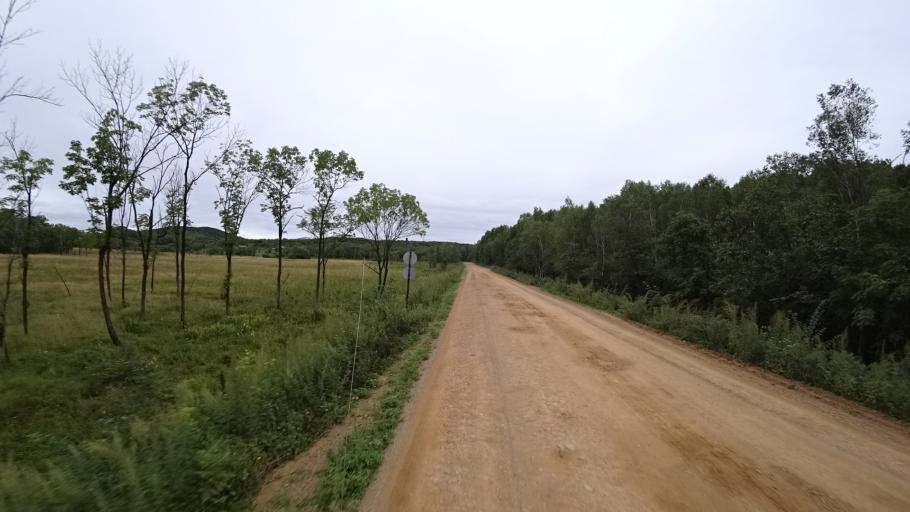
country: RU
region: Primorskiy
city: Rettikhovka
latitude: 44.1774
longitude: 132.8761
